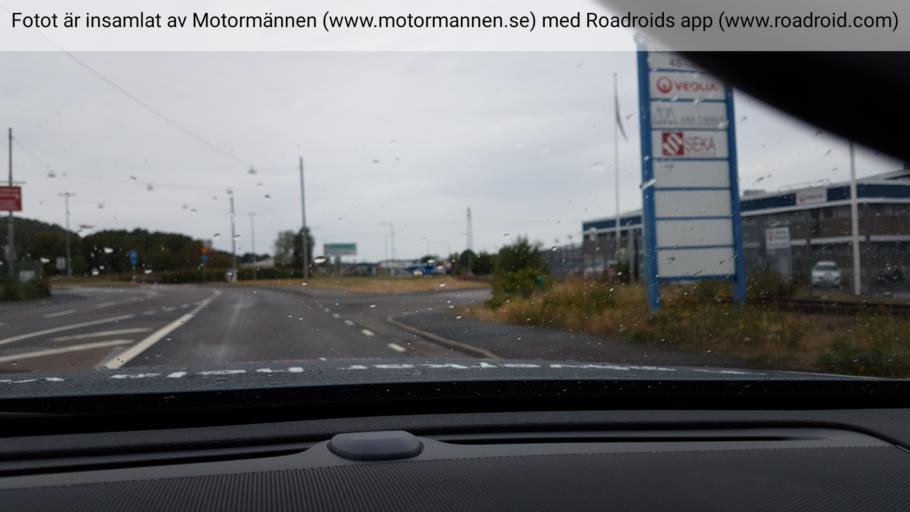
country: SE
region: Vaestra Goetaland
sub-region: Goteborg
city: Hammarkullen
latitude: 57.7576
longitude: 11.9962
